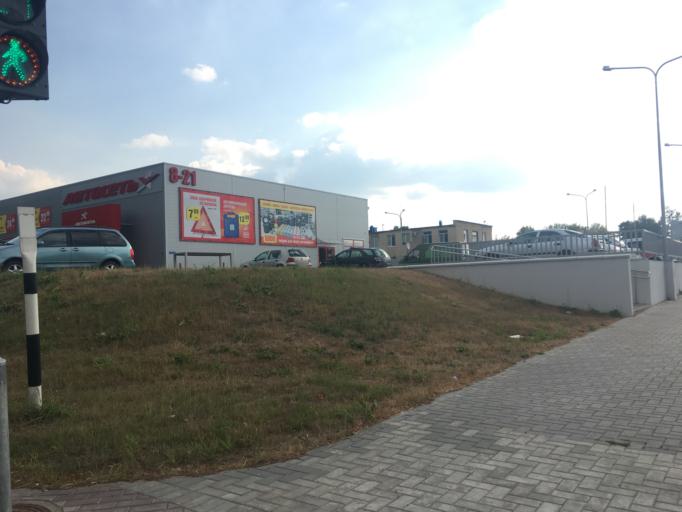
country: BY
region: Grodnenskaya
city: Hrodna
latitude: 53.6584
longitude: 23.8303
